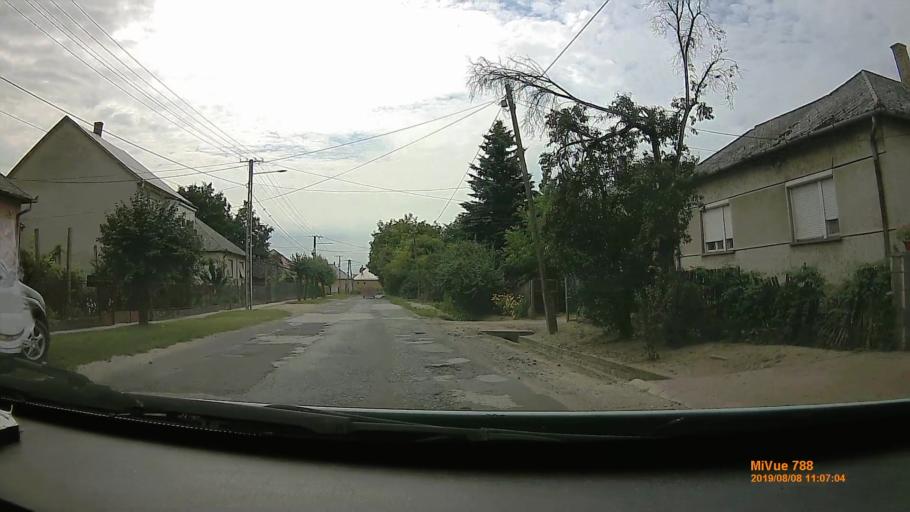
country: HU
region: Szabolcs-Szatmar-Bereg
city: Balkany
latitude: 47.7675
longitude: 21.8501
